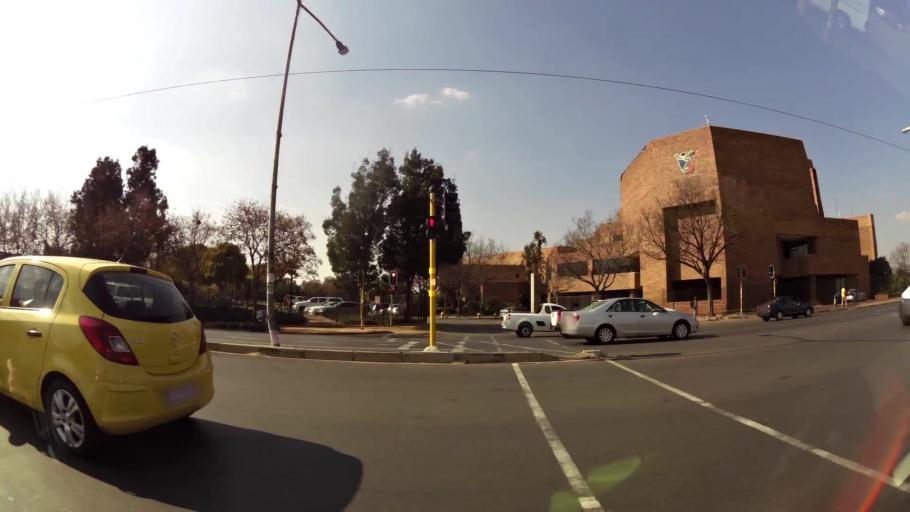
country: ZA
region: Gauteng
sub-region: City of Johannesburg Metropolitan Municipality
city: Modderfontein
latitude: -26.1020
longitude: 28.2265
